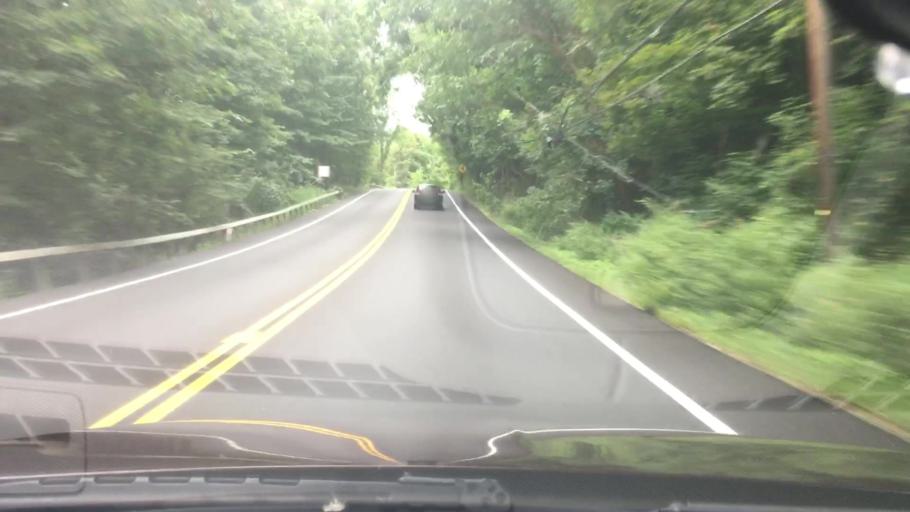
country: US
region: New York
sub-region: Dutchess County
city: Dover Plains
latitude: 41.8433
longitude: -73.5680
